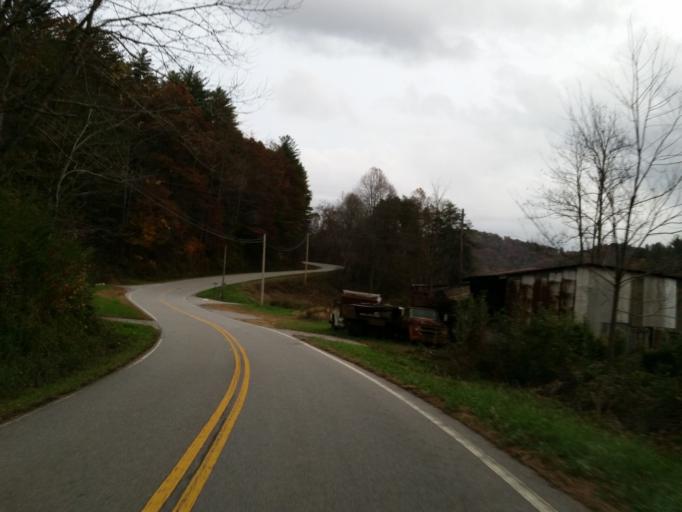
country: US
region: Georgia
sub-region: Lumpkin County
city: Dahlonega
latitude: 34.7077
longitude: -84.0708
